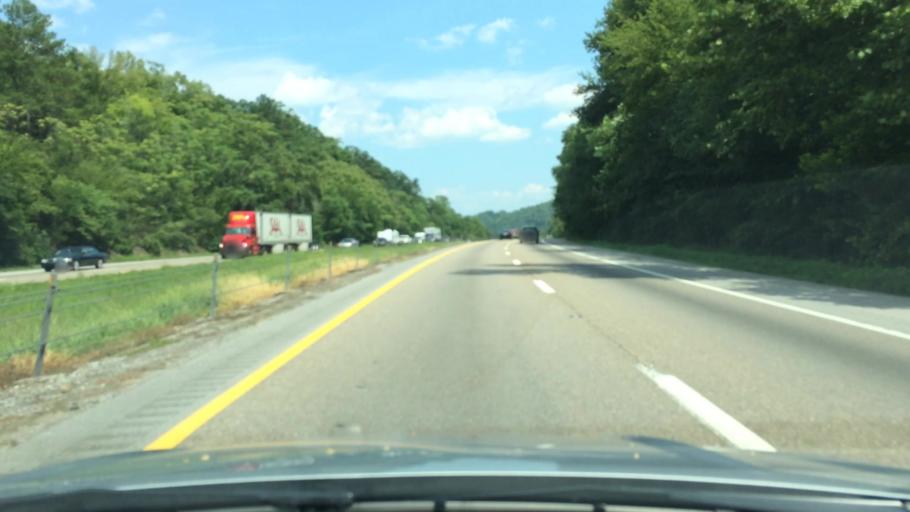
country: US
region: Tennessee
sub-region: Roane County
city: Kingston
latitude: 35.8632
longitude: -84.4141
